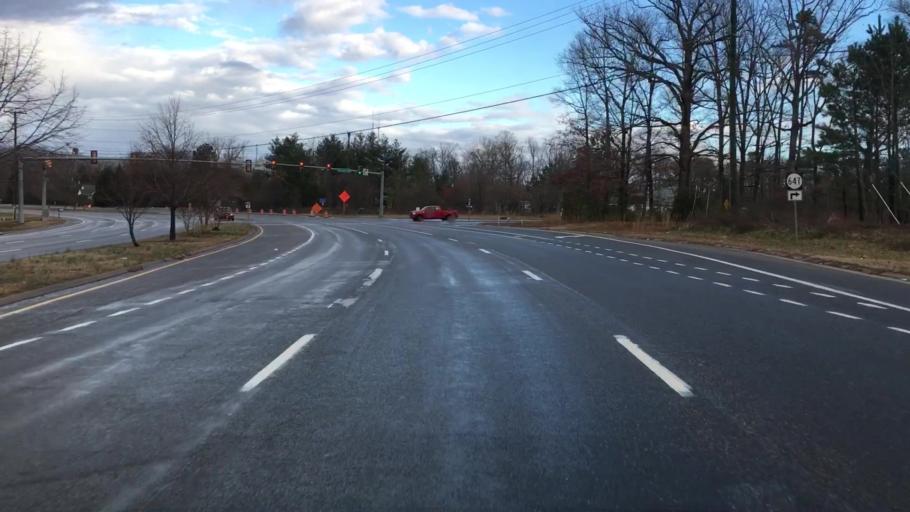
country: US
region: Virginia
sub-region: Chesterfield County
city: Bon Air
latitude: 37.4895
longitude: -77.5963
